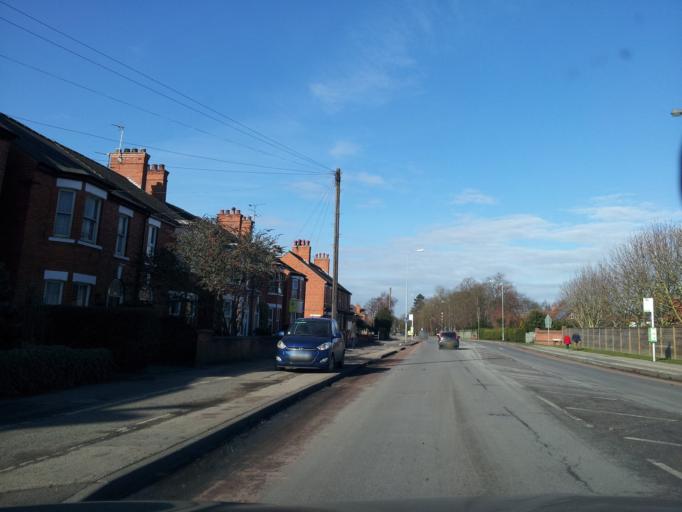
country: GB
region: England
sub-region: Nottinghamshire
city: Newark on Trent
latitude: 53.0635
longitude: -0.7894
